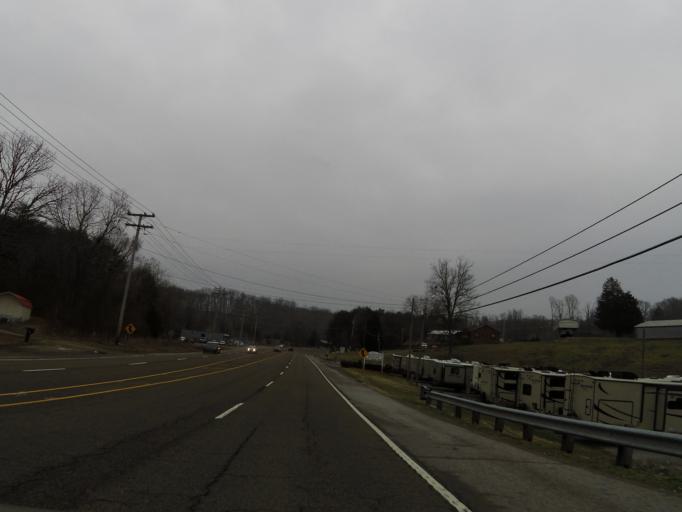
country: US
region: Tennessee
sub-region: Anderson County
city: Clinton
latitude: 36.0620
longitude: -84.1268
